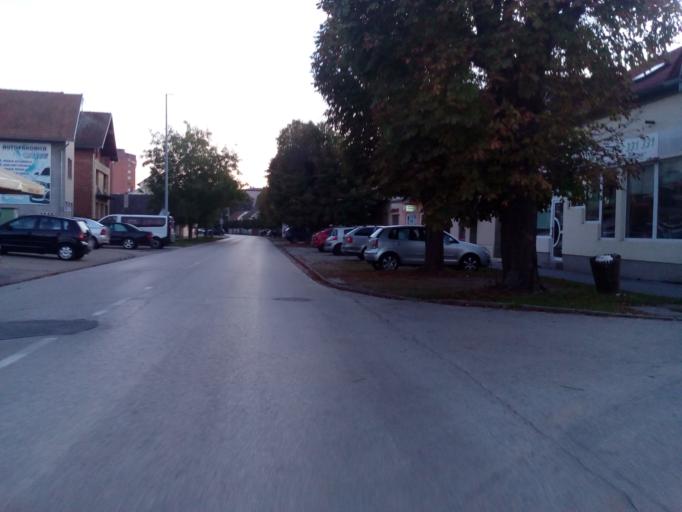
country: HR
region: Vukovarsko-Srijemska
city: Vinkovci
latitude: 45.2967
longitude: 18.8043
